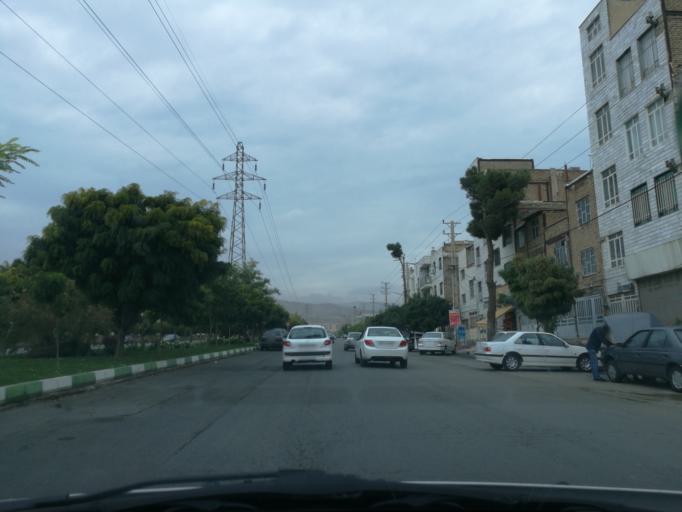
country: IR
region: Alborz
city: Karaj
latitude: 35.8538
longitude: 50.9200
